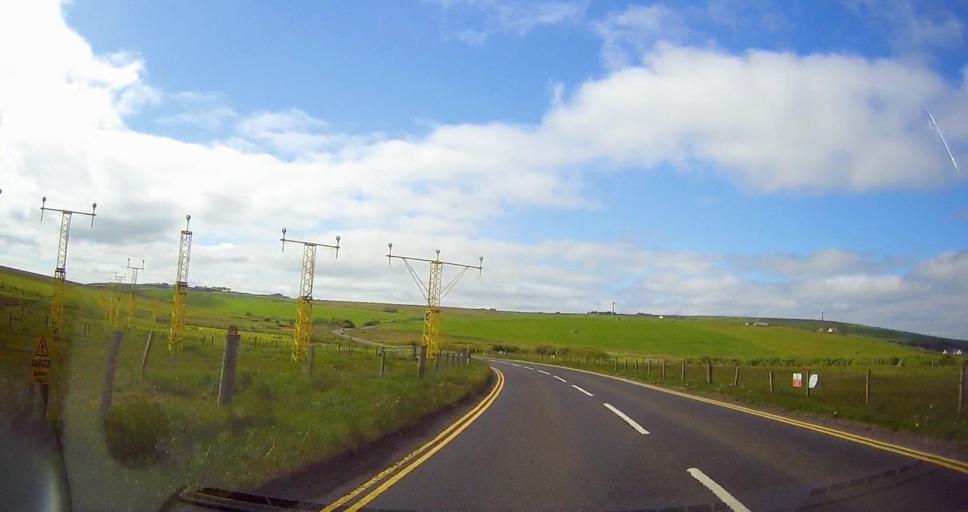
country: GB
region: Scotland
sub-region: Orkney Islands
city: Kirkwall
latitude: 58.9574
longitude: -2.9144
